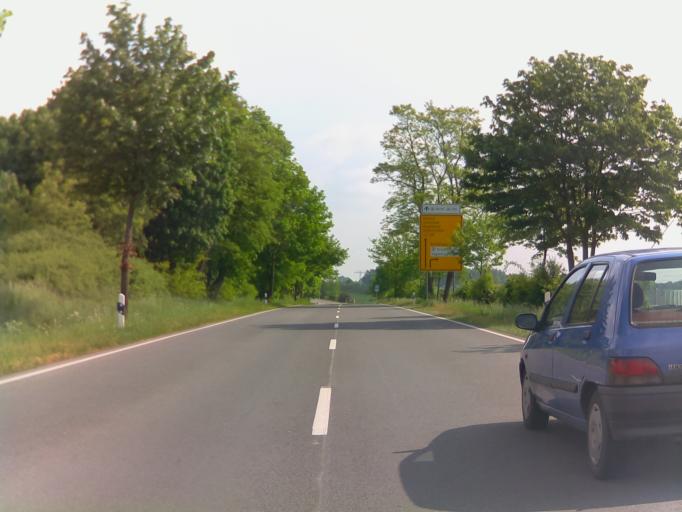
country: DE
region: Saxony-Anhalt
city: Gardelegen
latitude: 52.5216
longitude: 11.3522
